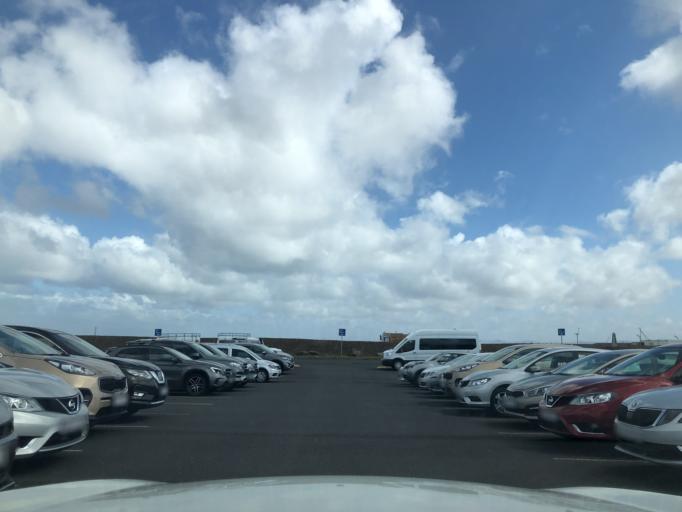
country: IS
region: Southern Peninsula
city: Reykjanesbaer
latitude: 63.9962
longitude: -22.6195
